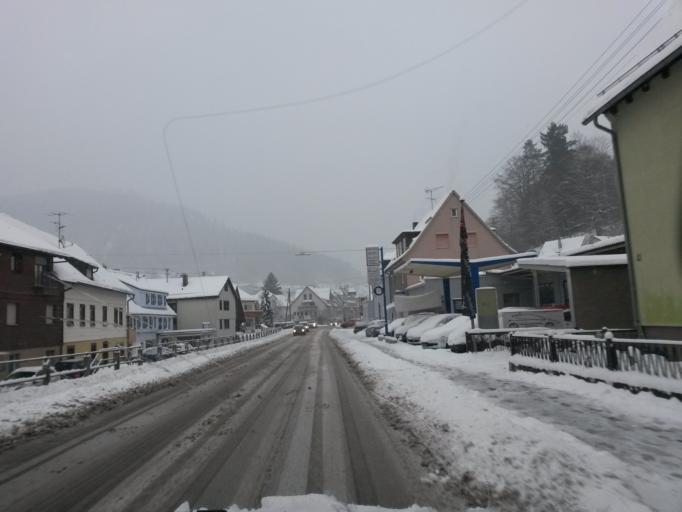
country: DE
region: Baden-Wuerttemberg
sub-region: Karlsruhe Region
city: Hofen an der Enz
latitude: 48.7755
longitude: 8.5719
